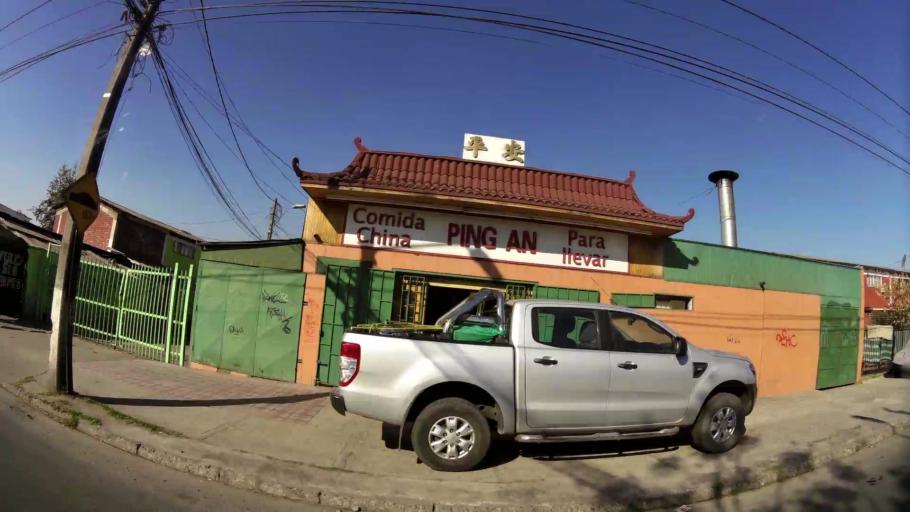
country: CL
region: Santiago Metropolitan
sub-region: Provincia de Santiago
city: La Pintana
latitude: -33.5606
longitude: -70.6109
